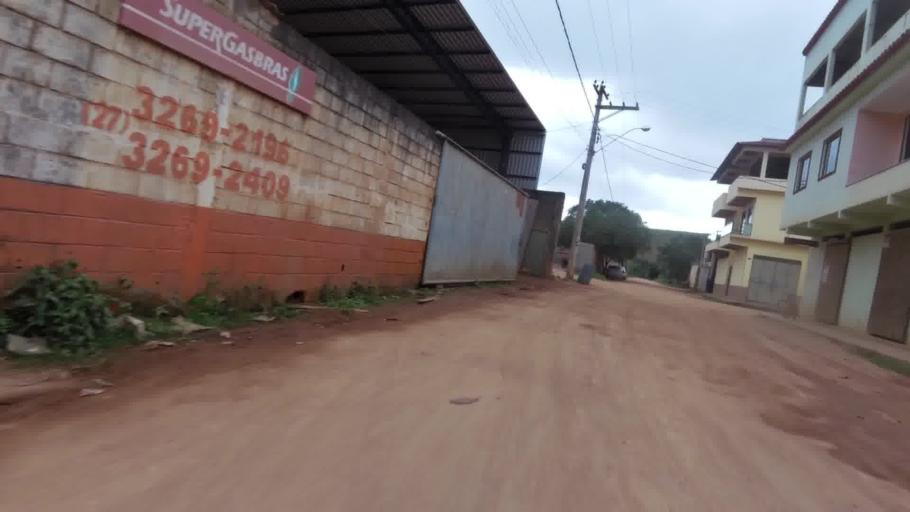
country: BR
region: Espirito Santo
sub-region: Alfredo Chaves
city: Alfredo Chaves
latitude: -20.6395
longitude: -40.7441
